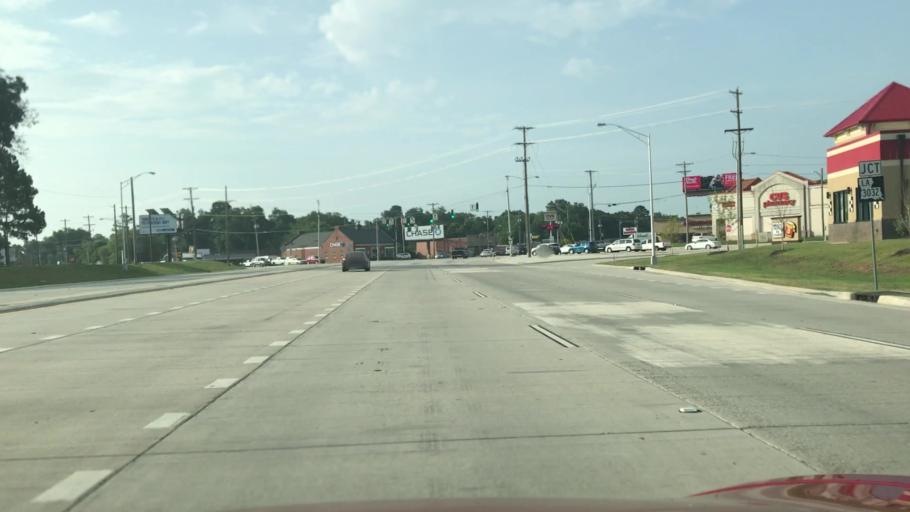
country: US
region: Louisiana
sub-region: Bossier Parish
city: Bossier City
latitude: 32.4814
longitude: -93.7229
